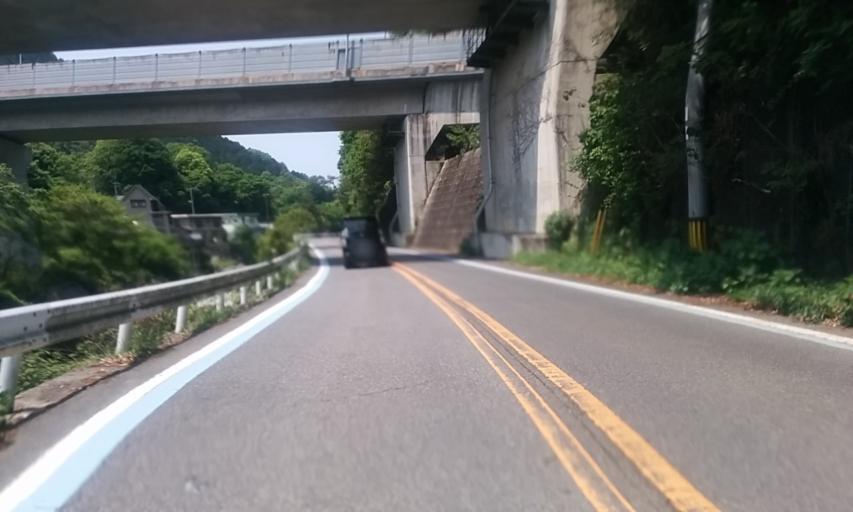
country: JP
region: Ehime
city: Niihama
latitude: 33.9178
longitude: 133.3127
